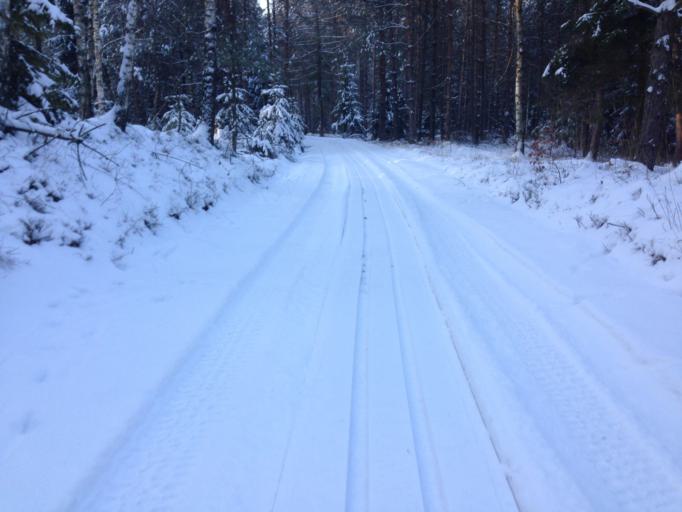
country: PL
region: Kujawsko-Pomorskie
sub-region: Powiat brodnicki
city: Gorzno
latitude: 53.1932
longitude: 19.6824
